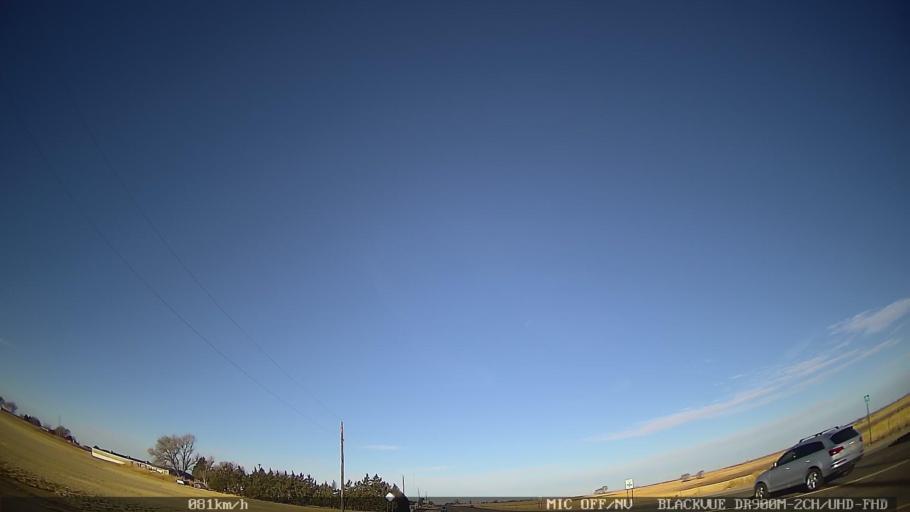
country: US
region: New Mexico
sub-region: Curry County
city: Clovis
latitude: 34.4340
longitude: -103.2331
